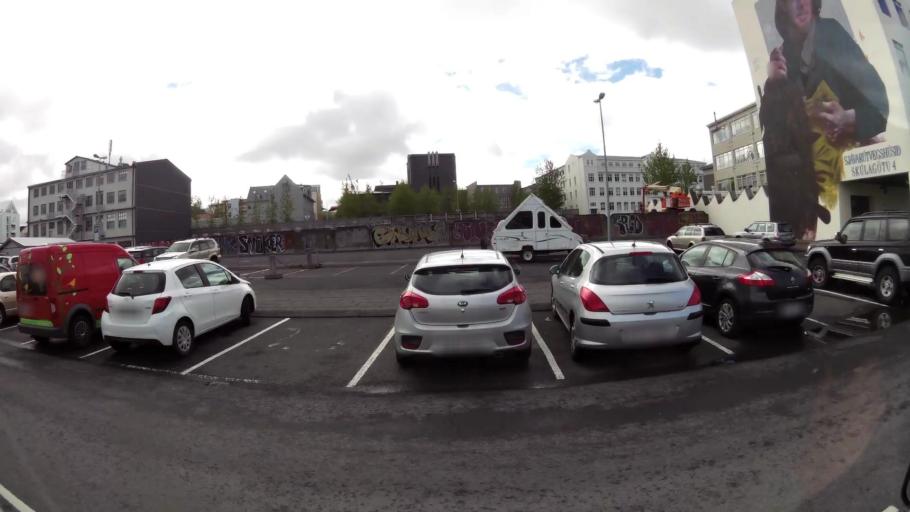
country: IS
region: Capital Region
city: Reykjavik
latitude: 64.1489
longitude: -21.9292
